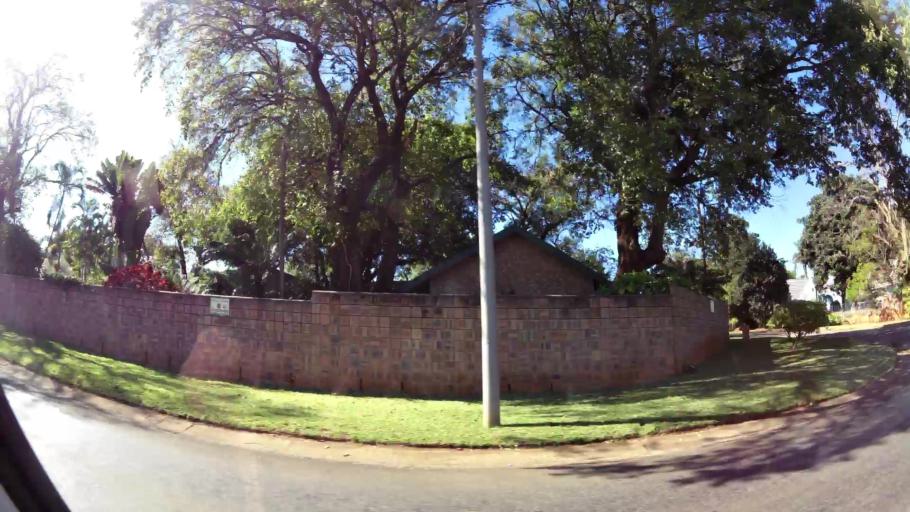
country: ZA
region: Limpopo
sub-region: Mopani District Municipality
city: Tzaneen
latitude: -23.8274
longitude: 30.1423
